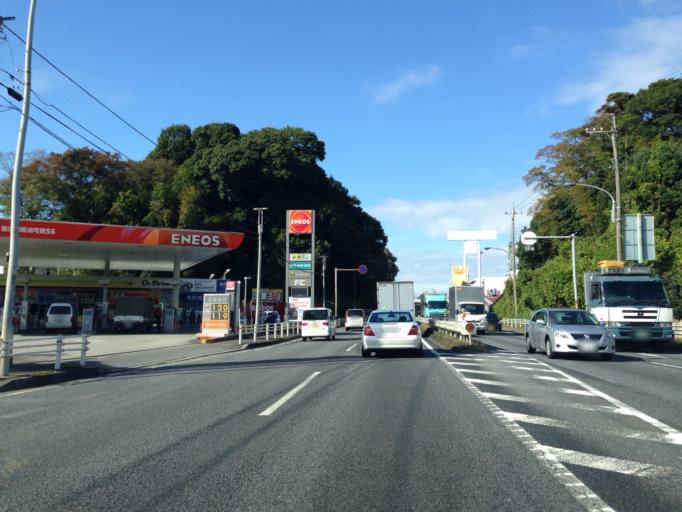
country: JP
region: Chiba
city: Kashiwa
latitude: 35.8741
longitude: 139.9708
